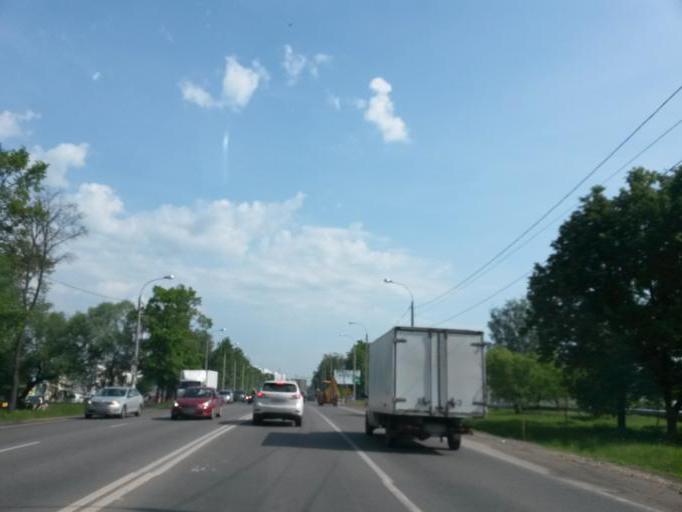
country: RU
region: Moskovskaya
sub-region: Chekhovskiy Rayon
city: Chekhov
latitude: 55.1588
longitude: 37.4646
